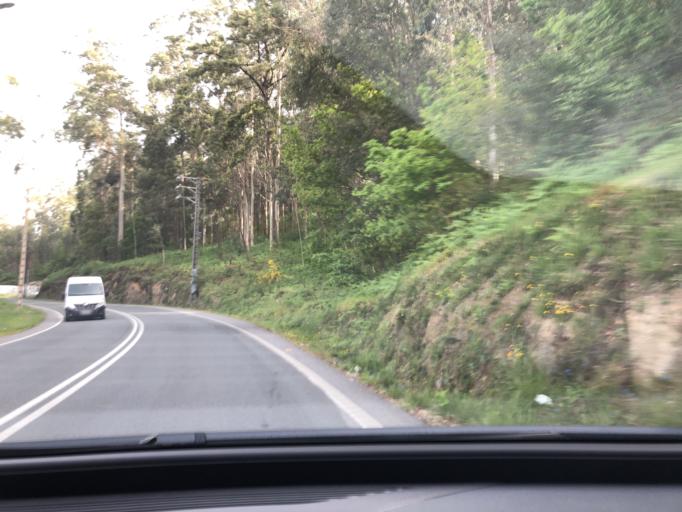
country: ES
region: Galicia
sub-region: Provincia de Pontevedra
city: Marin
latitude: 42.3758
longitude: -8.7244
